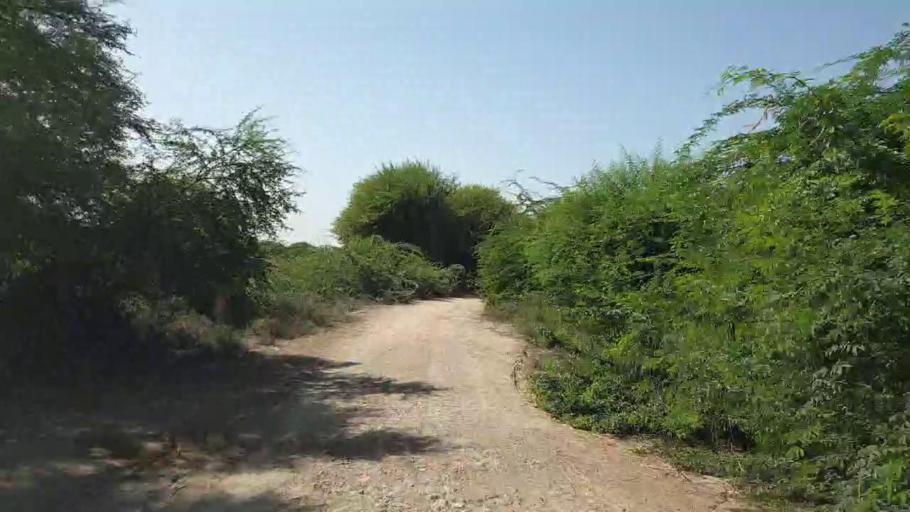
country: PK
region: Sindh
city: Tando Bago
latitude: 24.7068
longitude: 69.0463
